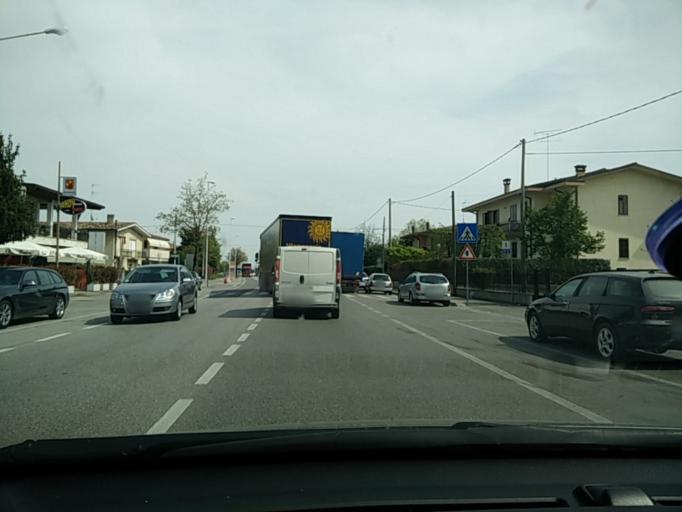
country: IT
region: Veneto
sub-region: Provincia di Treviso
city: San Vendemiano-Fossamerlo
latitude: 45.8790
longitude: 12.3288
